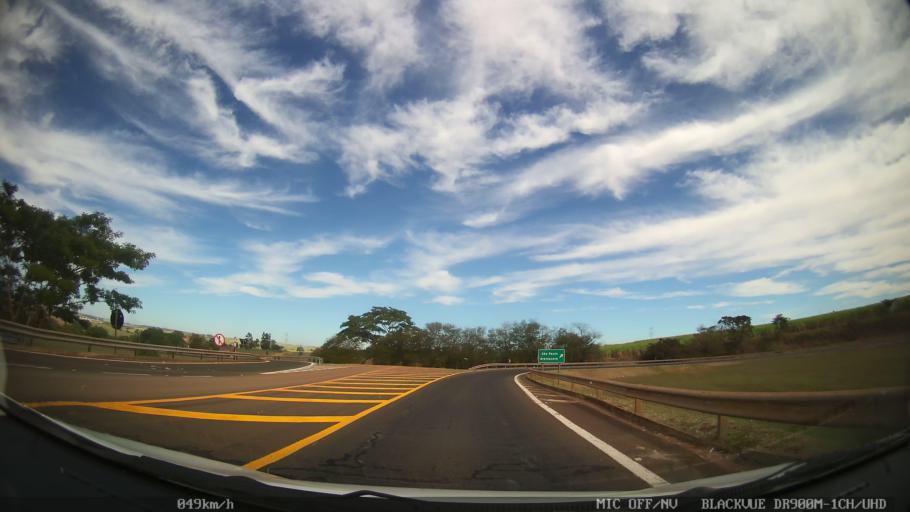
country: BR
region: Sao Paulo
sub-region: Taquaritinga
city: Taquaritinga
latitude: -21.5161
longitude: -48.5412
